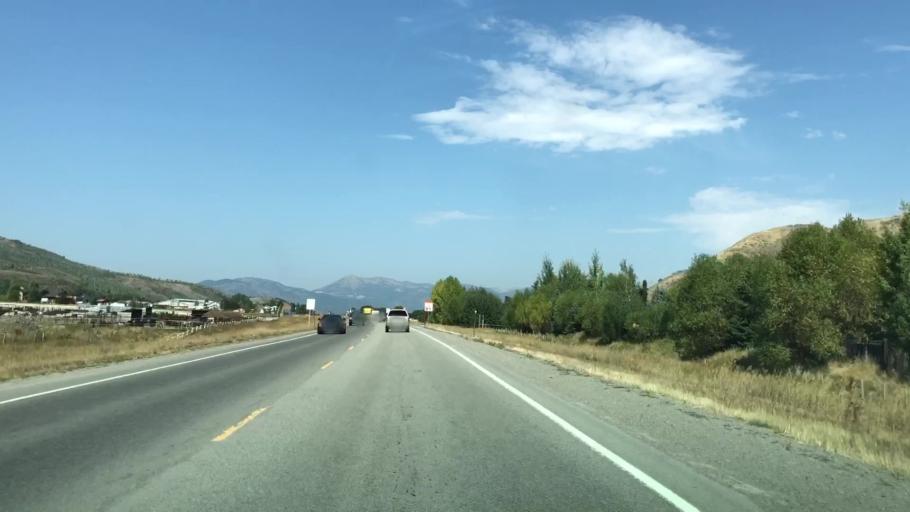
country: US
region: Wyoming
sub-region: Teton County
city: South Park
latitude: 43.3673
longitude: -110.7344
